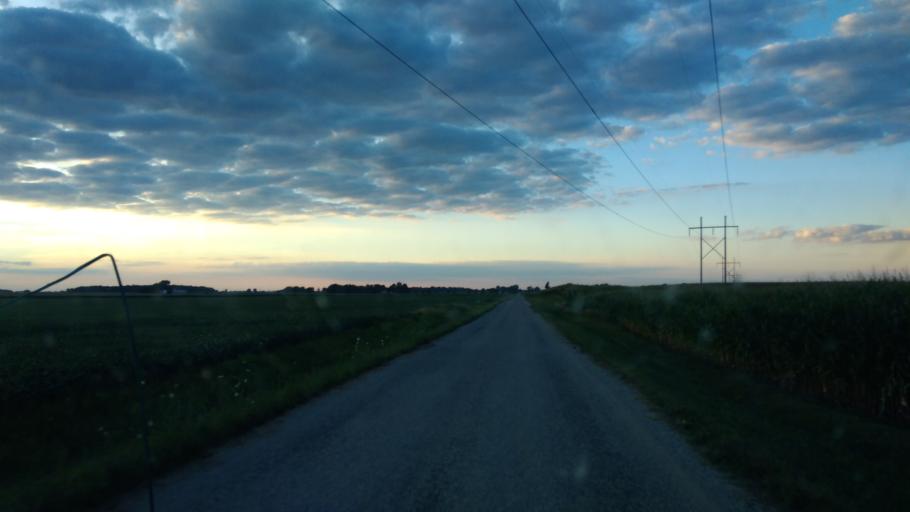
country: US
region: Indiana
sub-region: Adams County
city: Geneva
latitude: 40.6150
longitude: -85.0600
